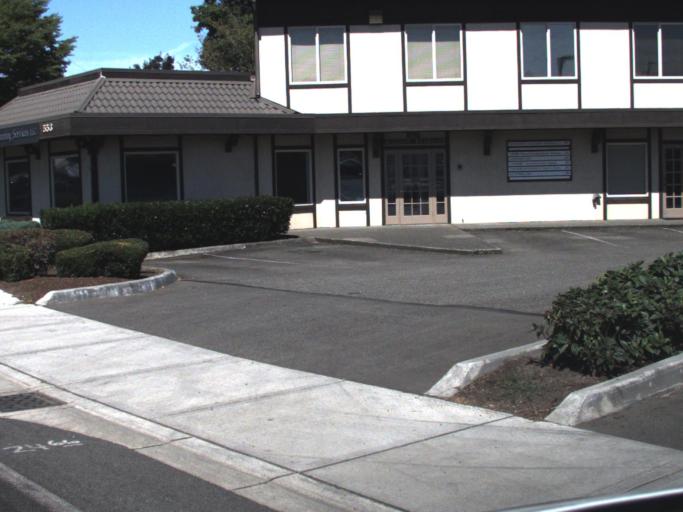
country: US
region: Washington
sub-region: King County
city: Enumclaw
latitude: 47.1994
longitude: -121.9852
